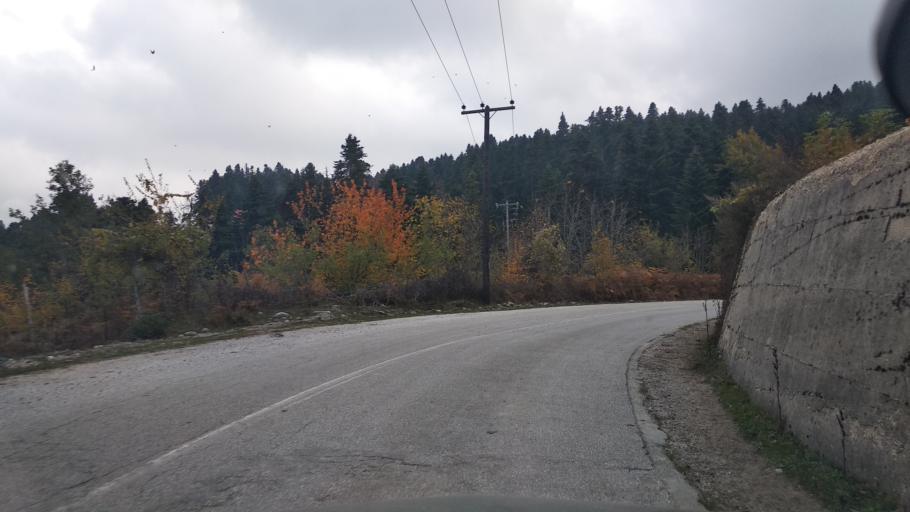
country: GR
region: Thessaly
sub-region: Trikala
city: Fiki
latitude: 39.5832
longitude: 21.4899
